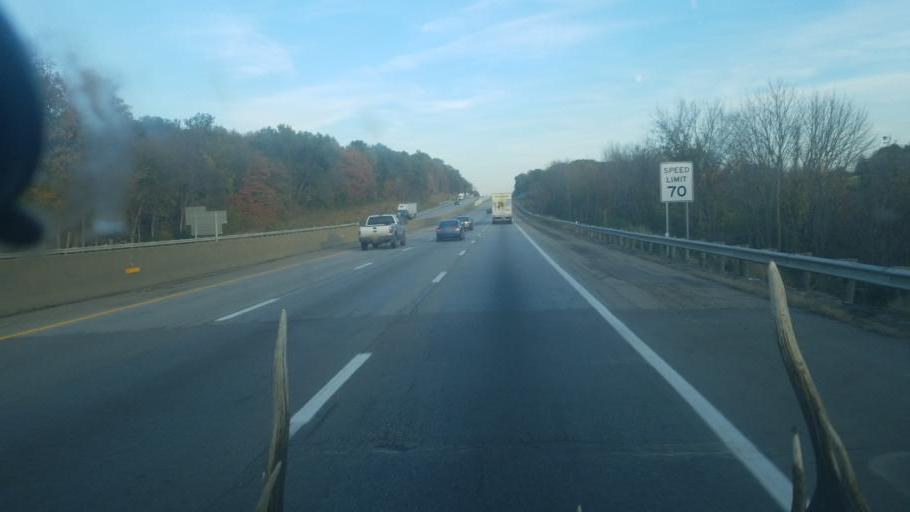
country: US
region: Ohio
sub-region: Perry County
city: Thornport
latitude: 39.9429
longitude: -82.3945
